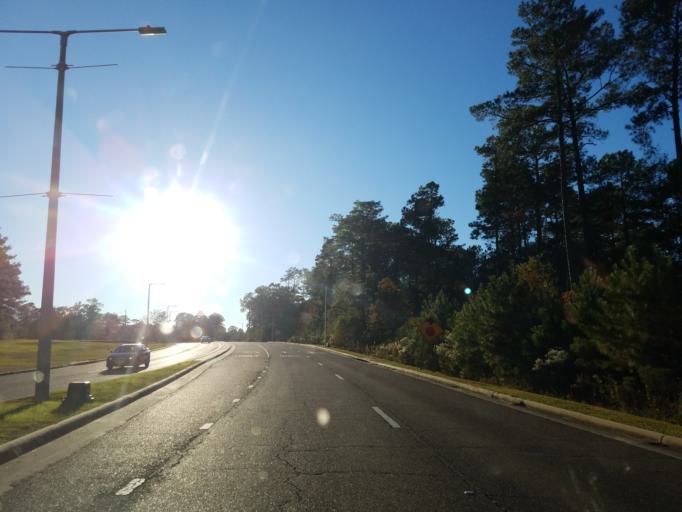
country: US
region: Mississippi
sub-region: Lamar County
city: Arnold Line
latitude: 31.3556
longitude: -89.3597
